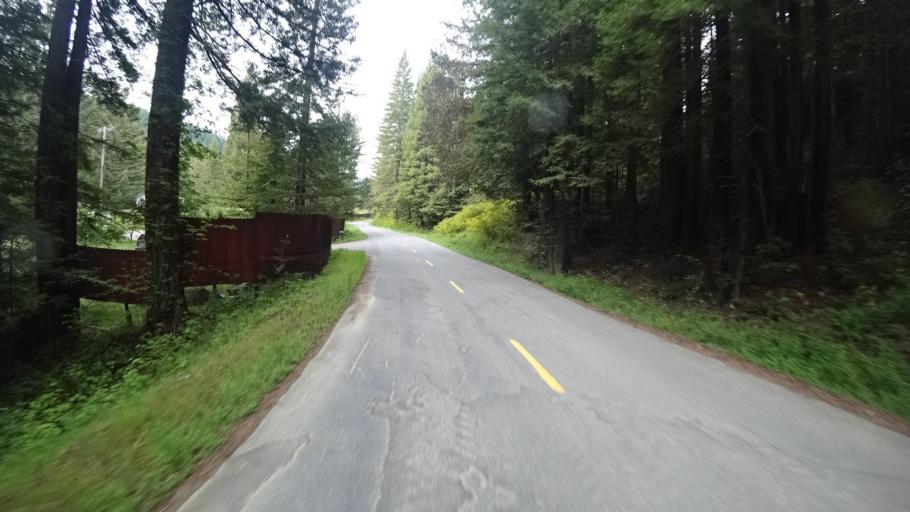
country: US
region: California
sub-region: Humboldt County
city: Redway
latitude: 40.2841
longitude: -123.8418
